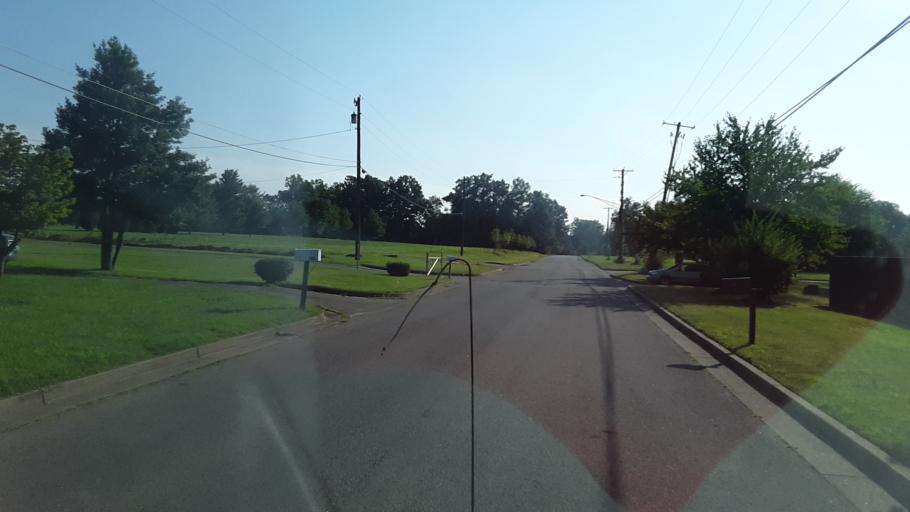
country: US
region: Kentucky
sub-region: Oldham County
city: La Grange
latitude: 38.4022
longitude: -85.3745
